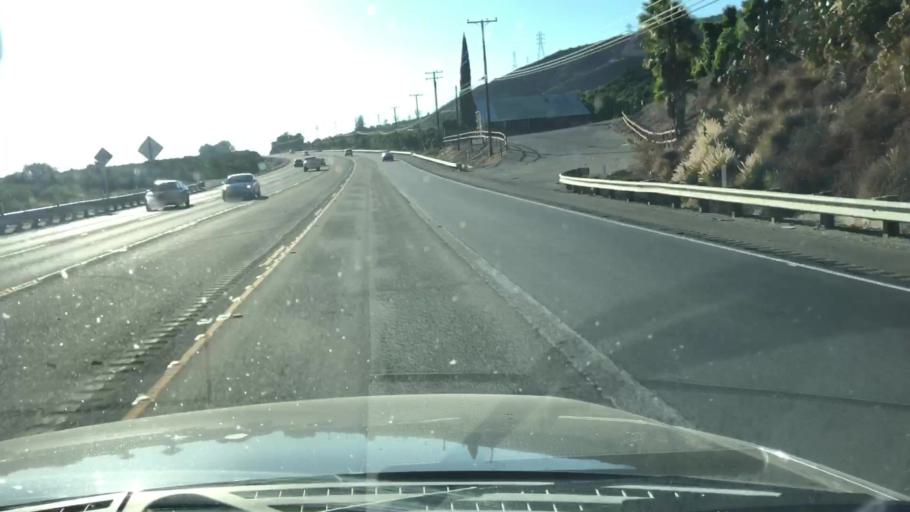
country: US
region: California
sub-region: Ventura County
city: Piru
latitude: 34.3971
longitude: -118.8539
